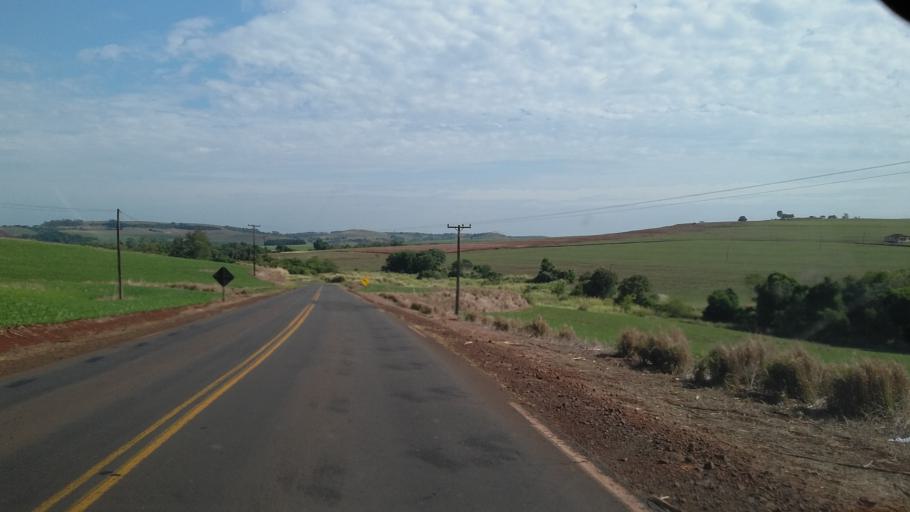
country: BR
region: Parana
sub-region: Cambara
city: Cambara
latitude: -23.1612
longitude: -50.1691
